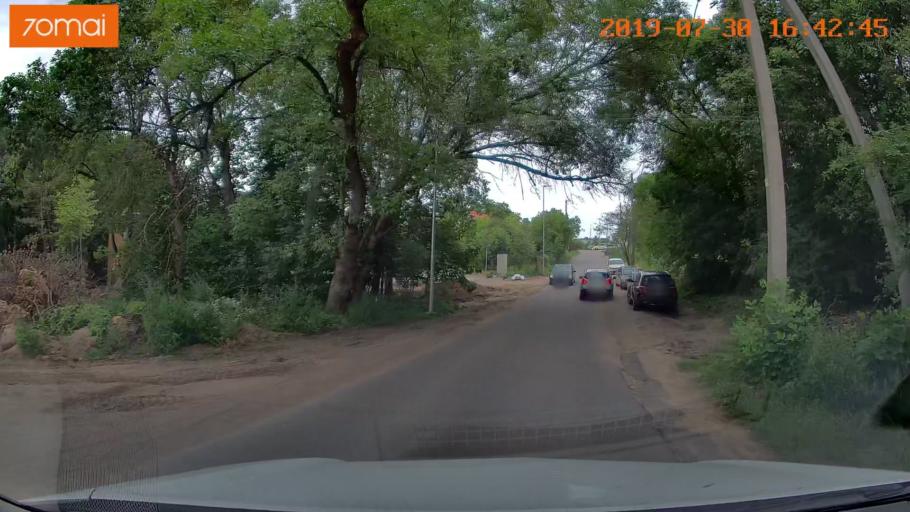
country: LT
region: Vilnius County
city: Rasos
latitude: 54.7172
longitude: 25.3516
